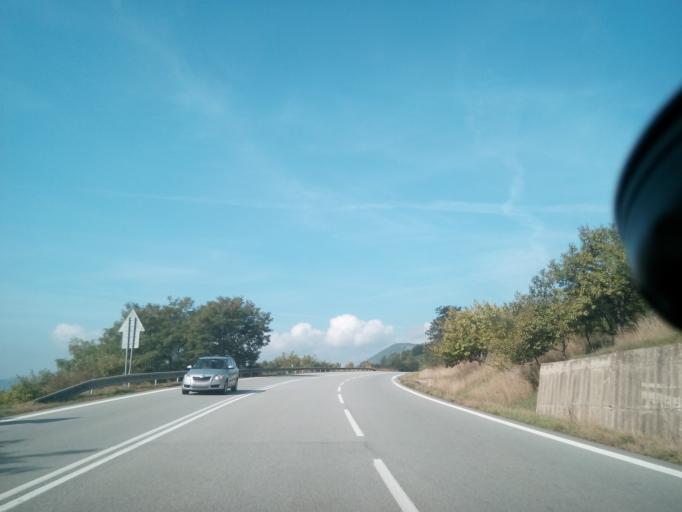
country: SK
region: Kosicky
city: Roznava
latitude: 48.5973
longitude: 20.6774
